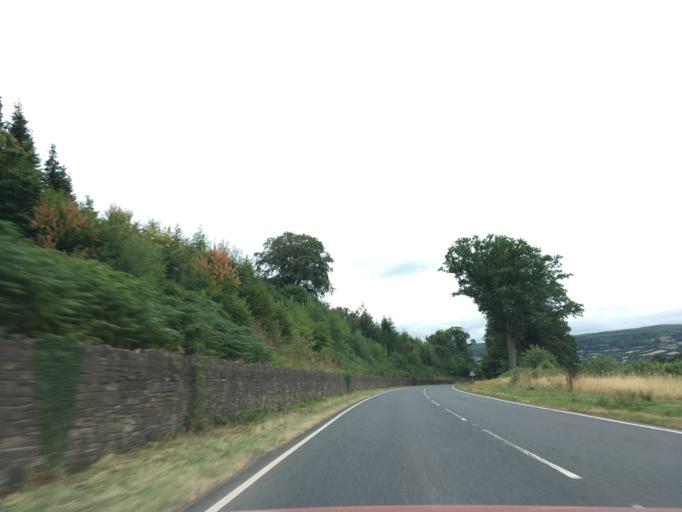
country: GB
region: Wales
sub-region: Blaenau Gwent
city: Brynmawr
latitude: 51.8783
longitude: -3.1860
